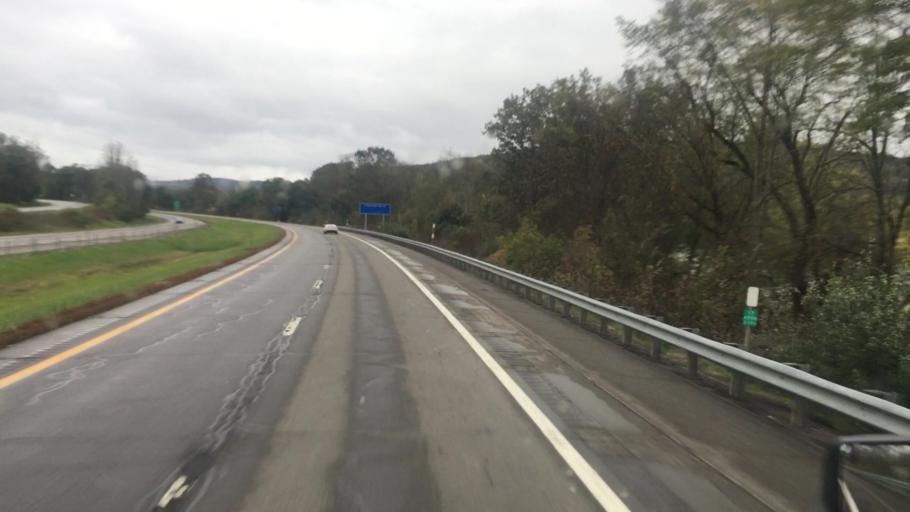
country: US
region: New York
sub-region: Tioga County
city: Owego
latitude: 42.0996
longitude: -76.2413
